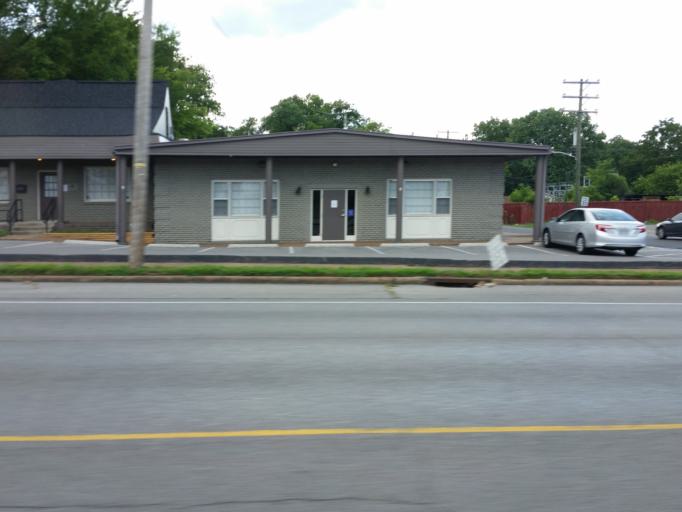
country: US
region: Tennessee
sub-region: Davidson County
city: Nashville
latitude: 36.2186
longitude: -86.7280
